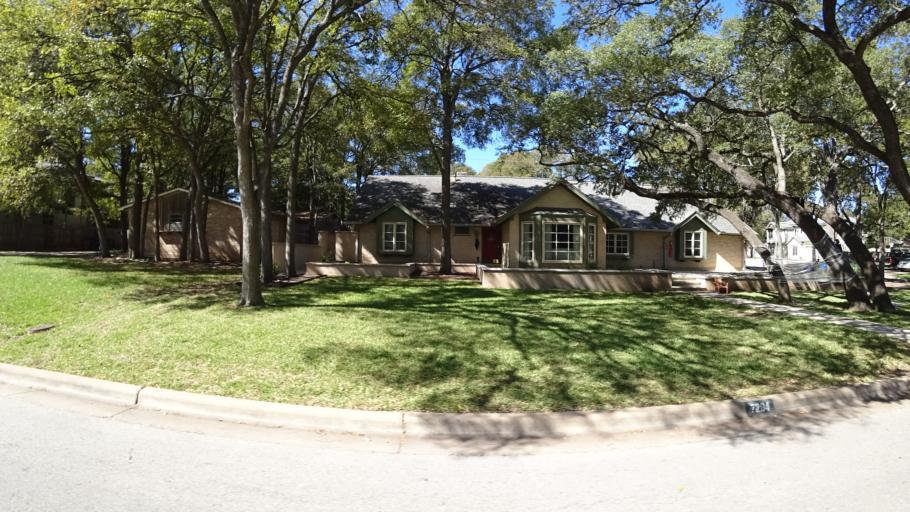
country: US
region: Texas
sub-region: Travis County
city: West Lake Hills
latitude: 30.3624
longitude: -97.7673
